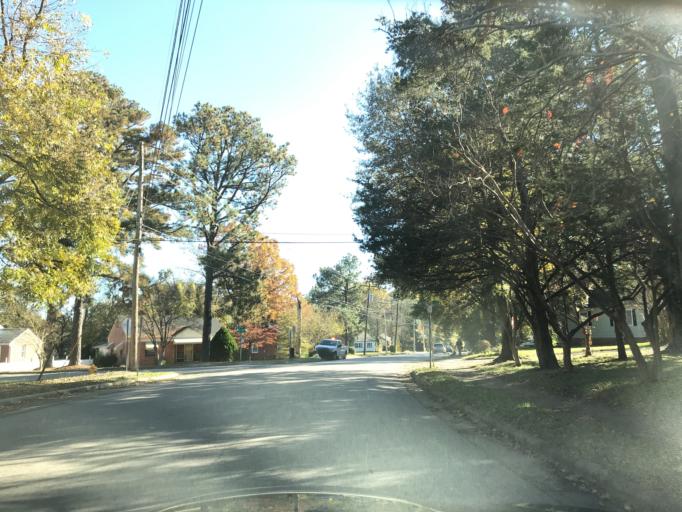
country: US
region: North Carolina
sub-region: Wake County
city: Raleigh
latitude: 35.7902
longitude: -78.6097
